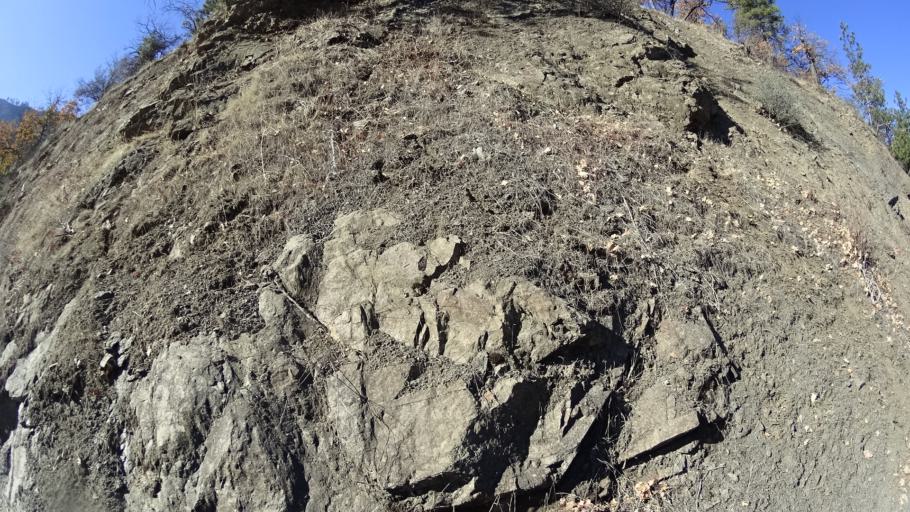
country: US
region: California
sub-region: Siskiyou County
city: Yreka
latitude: 41.8519
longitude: -122.6952
